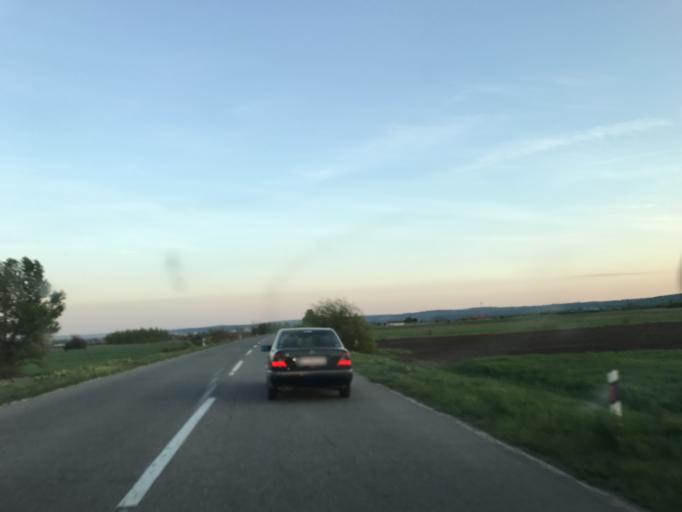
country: RS
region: Central Serbia
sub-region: Borski Okrug
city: Negotin
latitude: 44.2598
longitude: 22.5184
